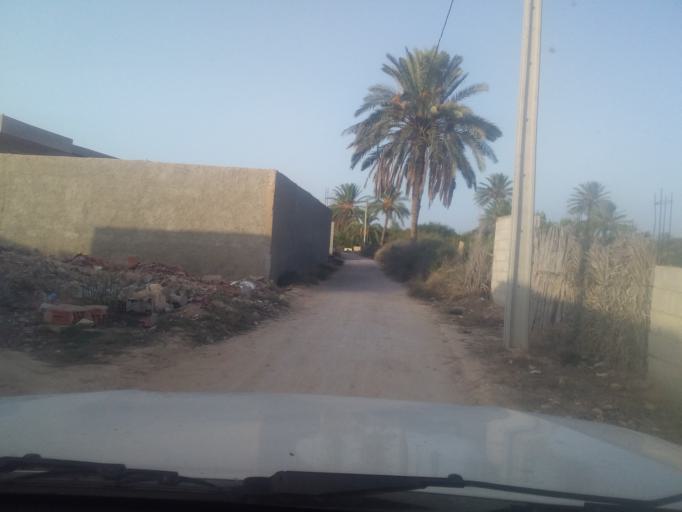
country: TN
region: Qabis
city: Gabes
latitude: 33.6291
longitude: 10.2903
